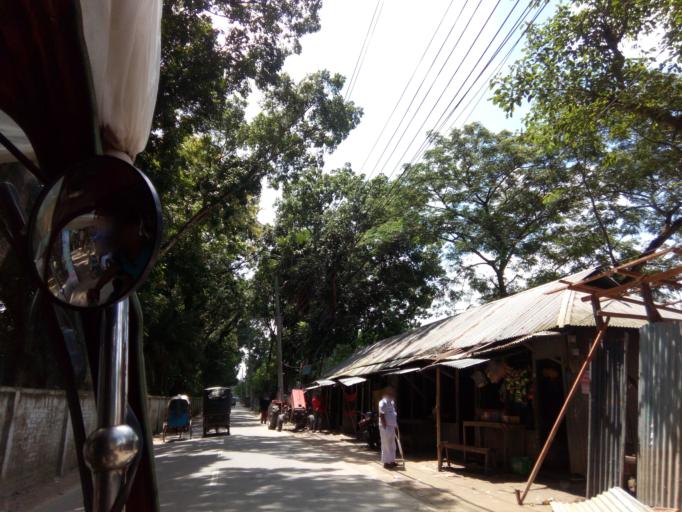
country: BD
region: Dhaka
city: Tungipara
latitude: 22.9961
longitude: 89.8140
